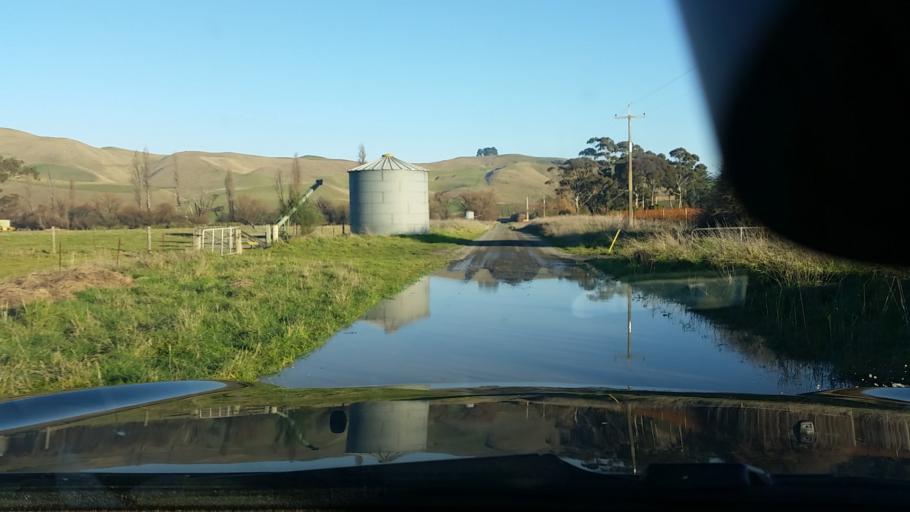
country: NZ
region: Marlborough
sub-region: Marlborough District
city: Blenheim
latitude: -41.6796
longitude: 174.0386
